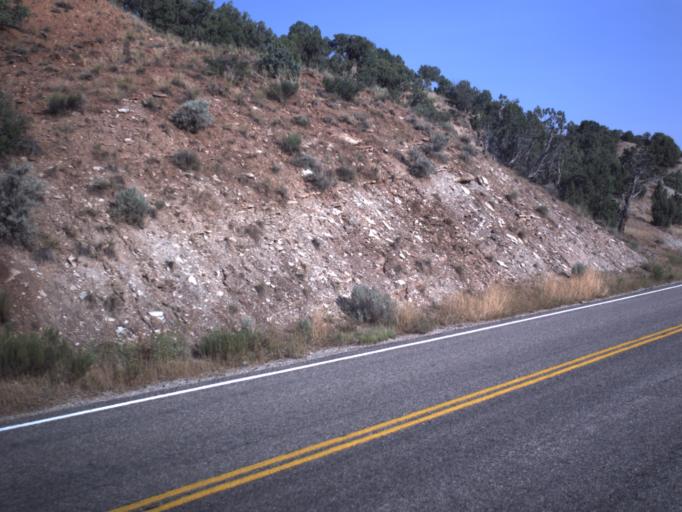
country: US
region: Utah
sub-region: Uintah County
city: Vernal
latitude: 40.6010
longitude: -109.4660
